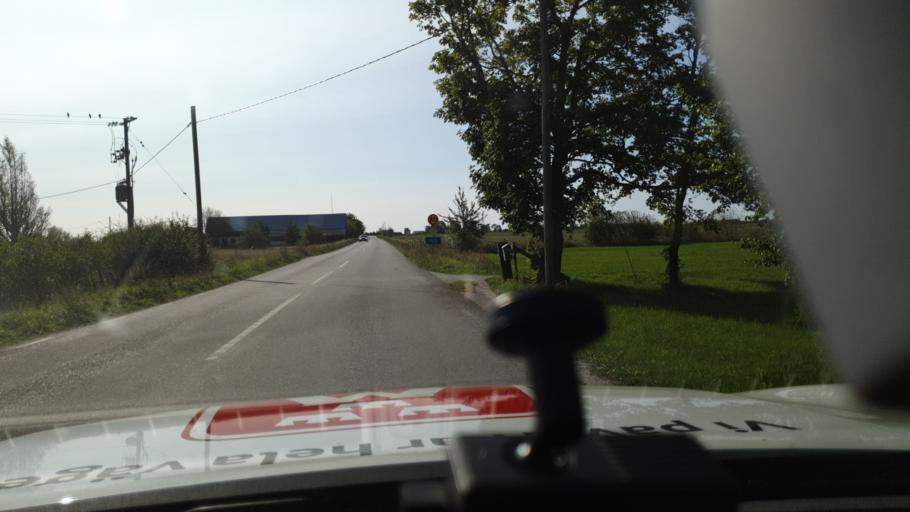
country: SE
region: Gotland
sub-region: Gotland
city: Hemse
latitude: 57.1502
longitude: 18.2840
